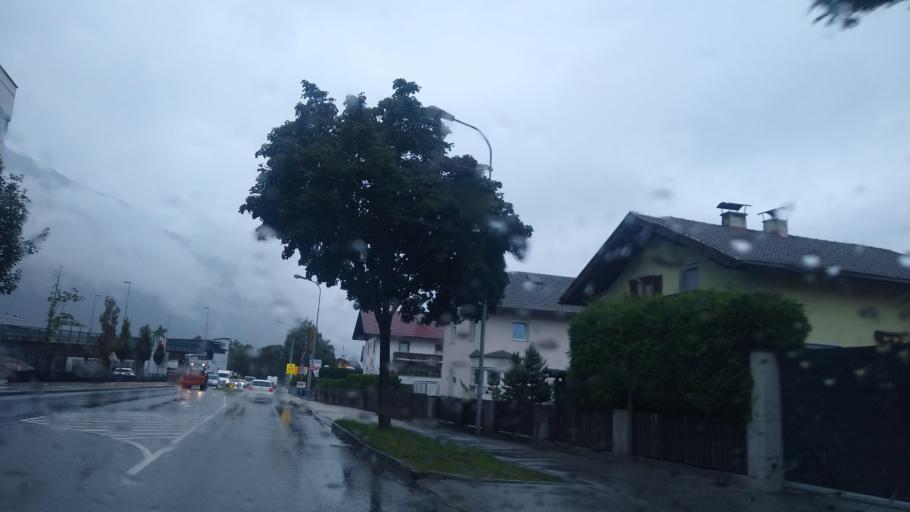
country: AT
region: Tyrol
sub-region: Politischer Bezirk Schwaz
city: Schwaz
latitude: 47.3524
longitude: 11.7069
